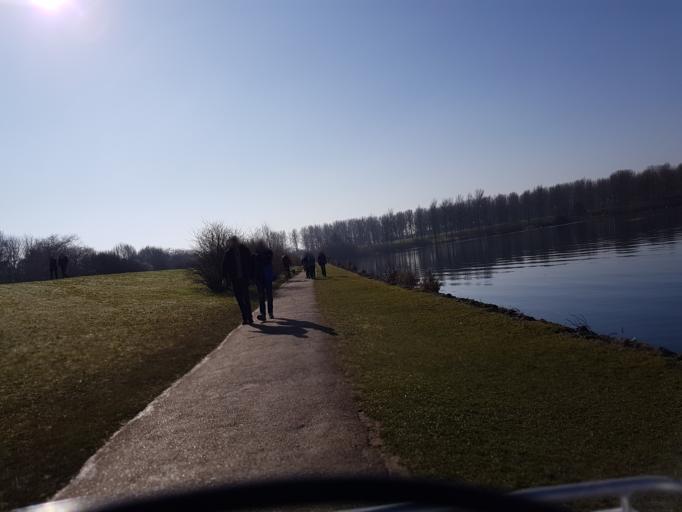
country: GB
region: England
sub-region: Milton Keynes
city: Broughton
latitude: 52.0506
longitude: -0.7138
